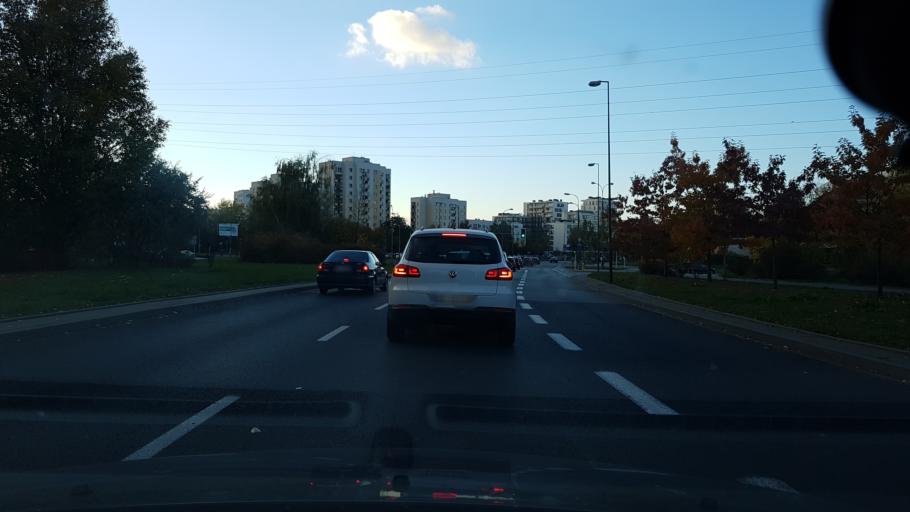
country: PL
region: Masovian Voivodeship
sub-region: Warszawa
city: Ursynow
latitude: 52.1562
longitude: 21.0461
